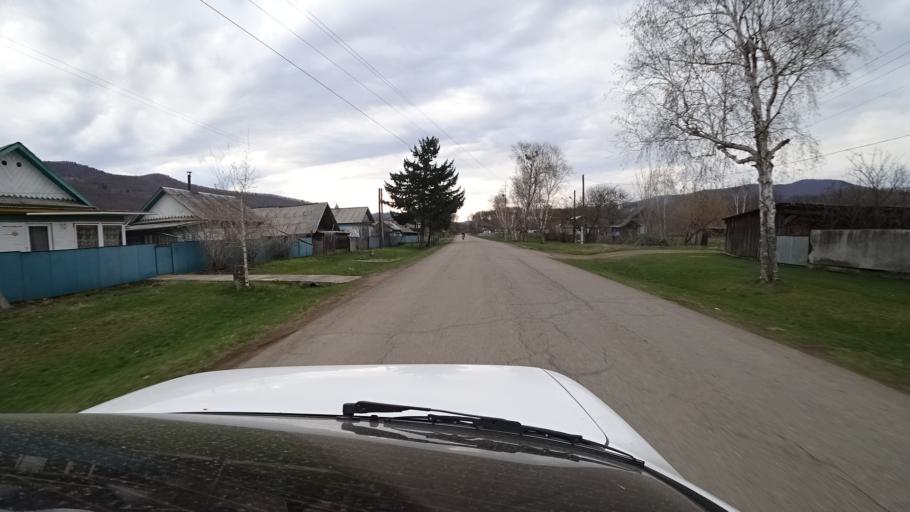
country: RU
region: Primorskiy
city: Novopokrovka
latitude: 45.1446
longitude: 134.3848
